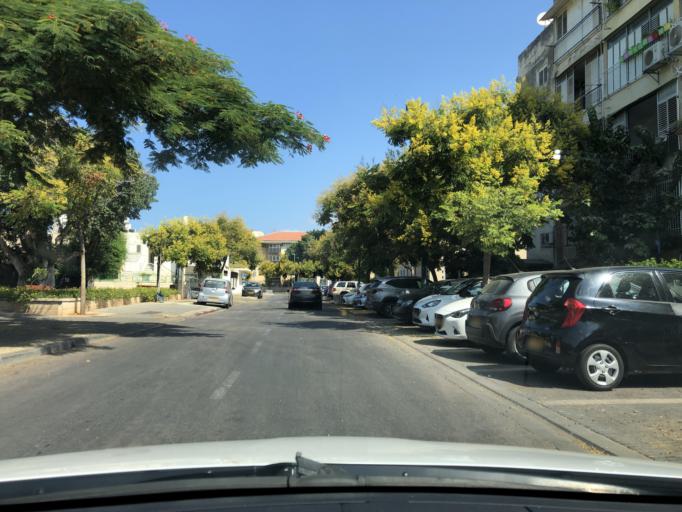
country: IL
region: Tel Aviv
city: Yafo
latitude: 32.0429
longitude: 34.7566
